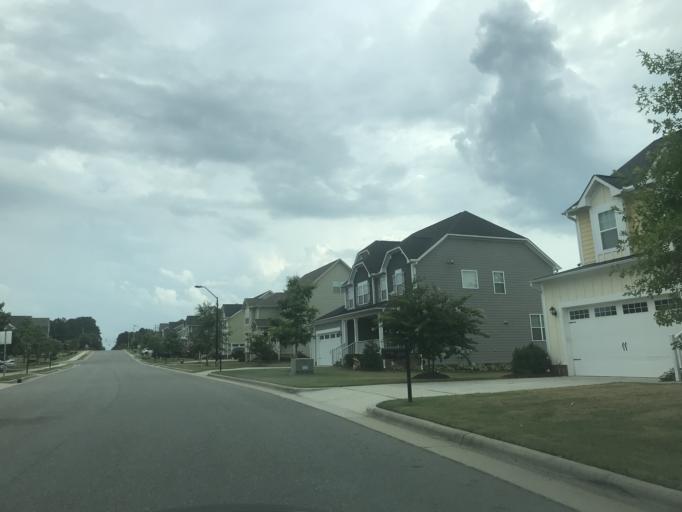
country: US
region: North Carolina
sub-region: Wake County
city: Knightdale
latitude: 35.8368
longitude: -78.5555
